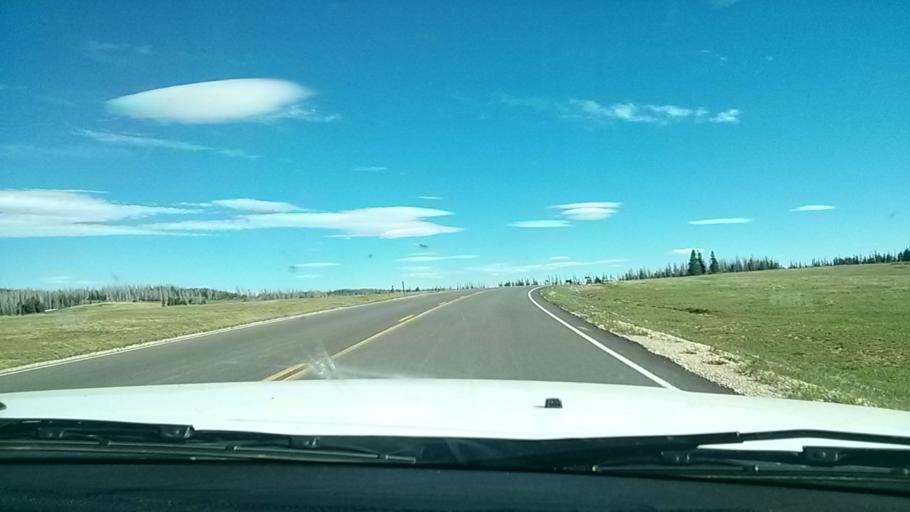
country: US
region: Utah
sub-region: Iron County
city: Parowan
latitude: 37.6672
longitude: -112.8386
